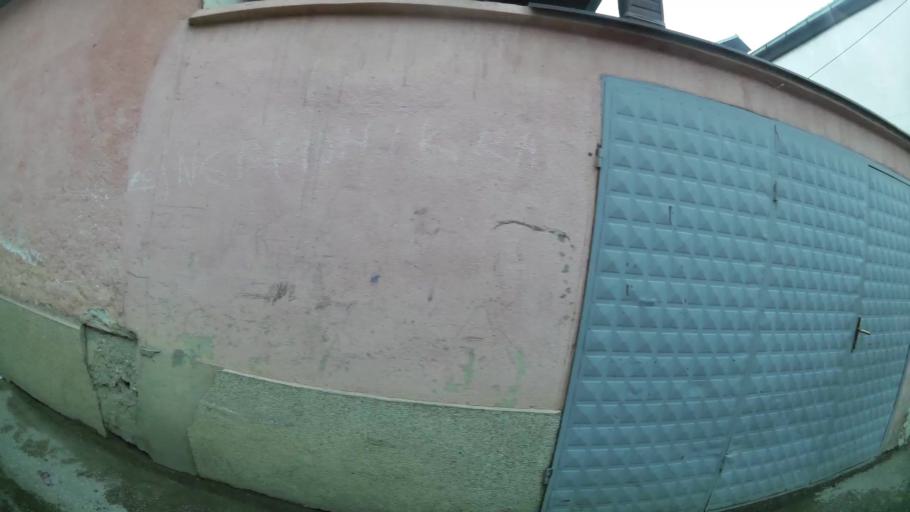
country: MK
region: Cair
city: Cair
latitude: 42.0076
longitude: 21.4444
